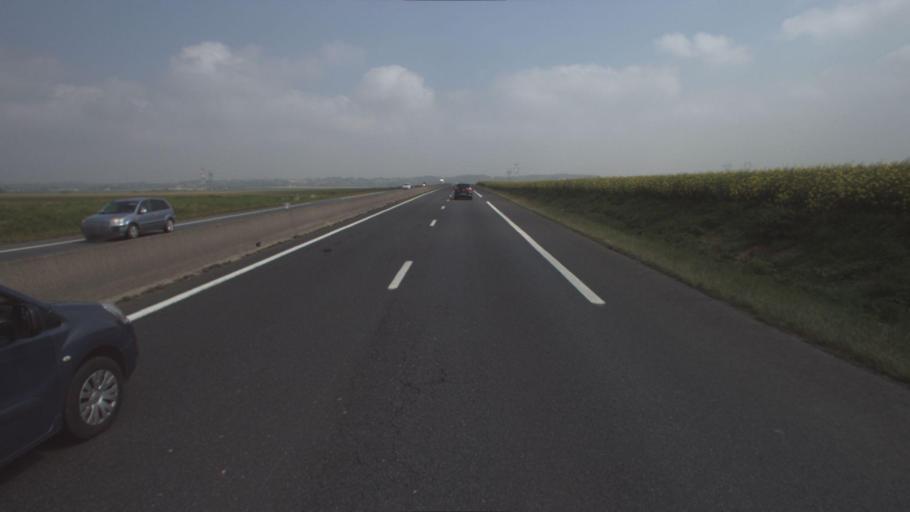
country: FR
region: Ile-de-France
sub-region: Departement de Seine-et-Marne
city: Longperrier
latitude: 49.0243
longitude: 2.6669
